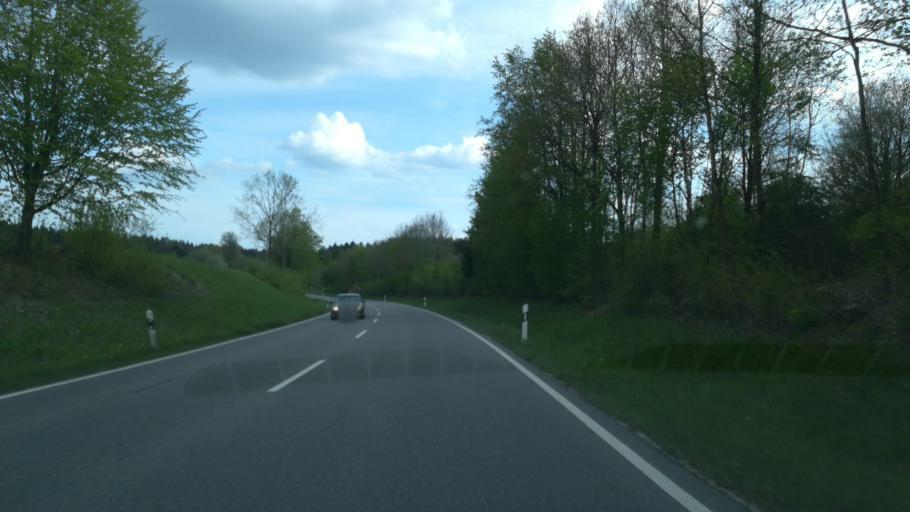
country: DE
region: Baden-Wuerttemberg
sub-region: Tuebingen Region
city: Messkirch
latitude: 47.9852
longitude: 9.0785
